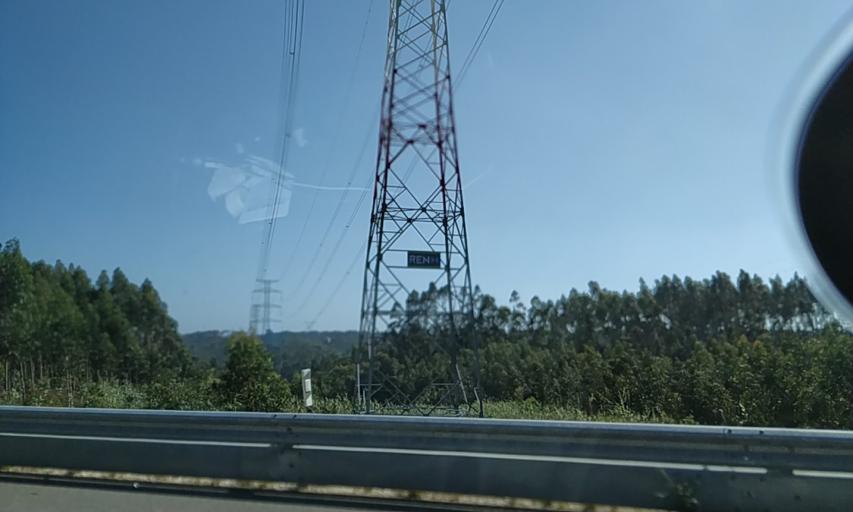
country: PT
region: Coimbra
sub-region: Figueira da Foz
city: Alhadas
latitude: 40.1553
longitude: -8.7716
